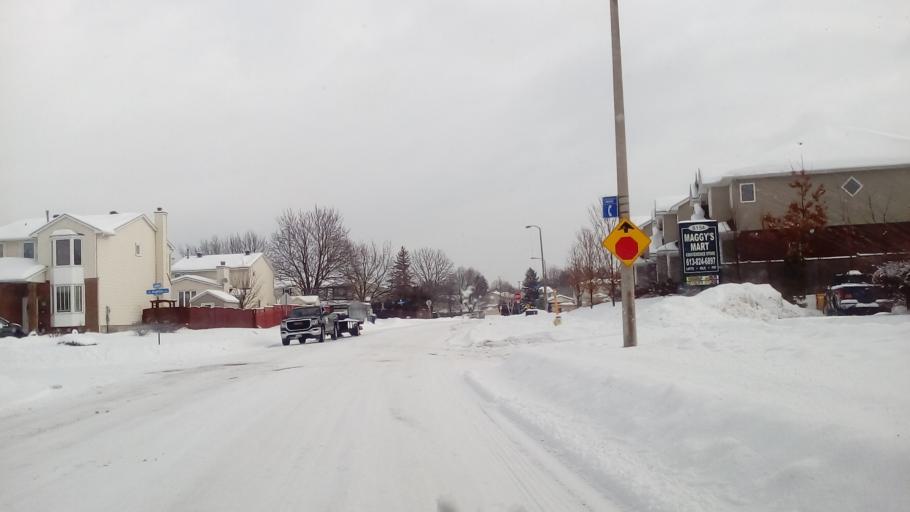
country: CA
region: Quebec
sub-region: Outaouais
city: Gatineau
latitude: 45.4878
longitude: -75.5118
